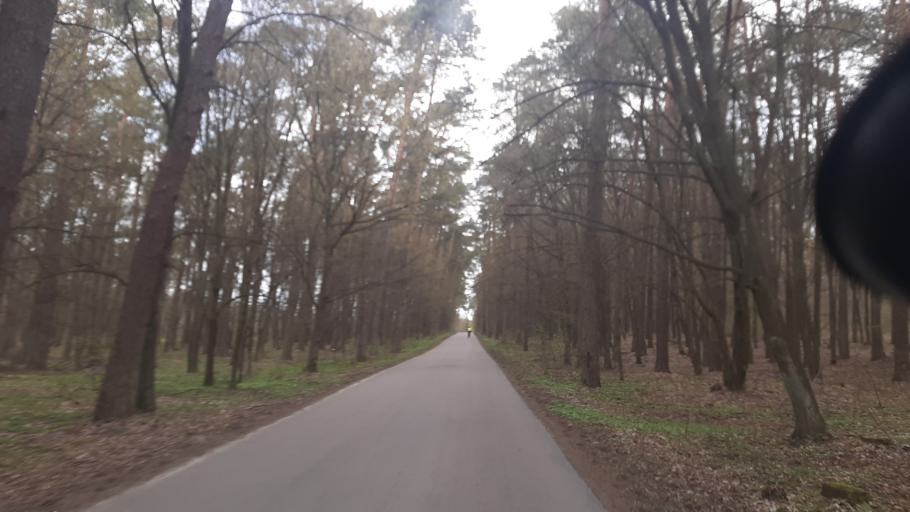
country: PL
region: Lublin Voivodeship
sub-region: Powiat lubelski
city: Niemce
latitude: 51.3722
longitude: 22.5525
